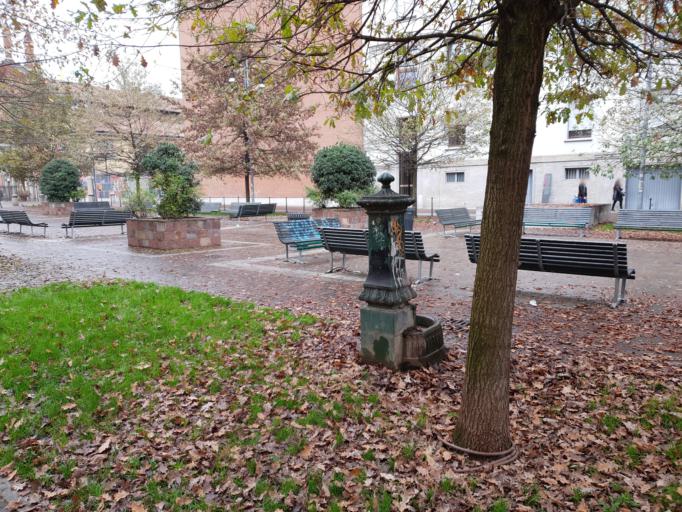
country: IT
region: Lombardy
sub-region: Citta metropolitana di Milano
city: Milano
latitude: 45.4559
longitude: 9.1925
